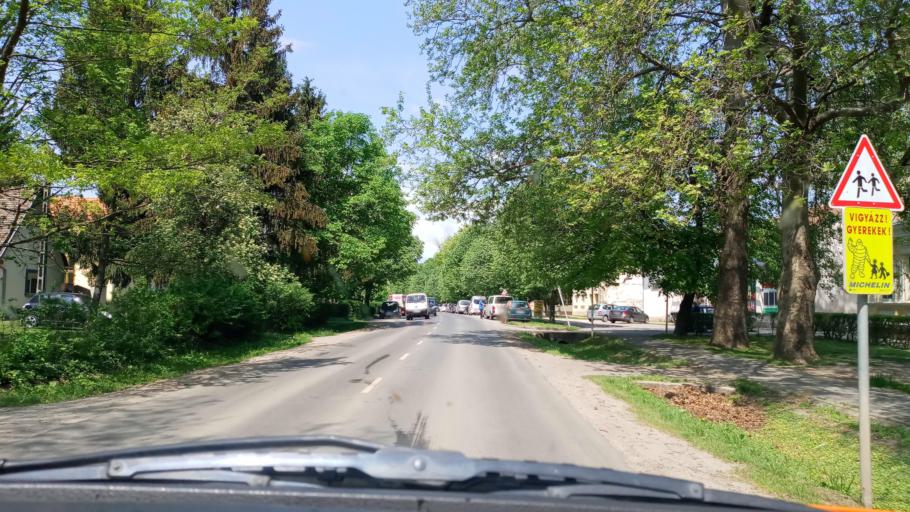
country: HU
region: Baranya
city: Boly
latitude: 45.9658
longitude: 18.5203
